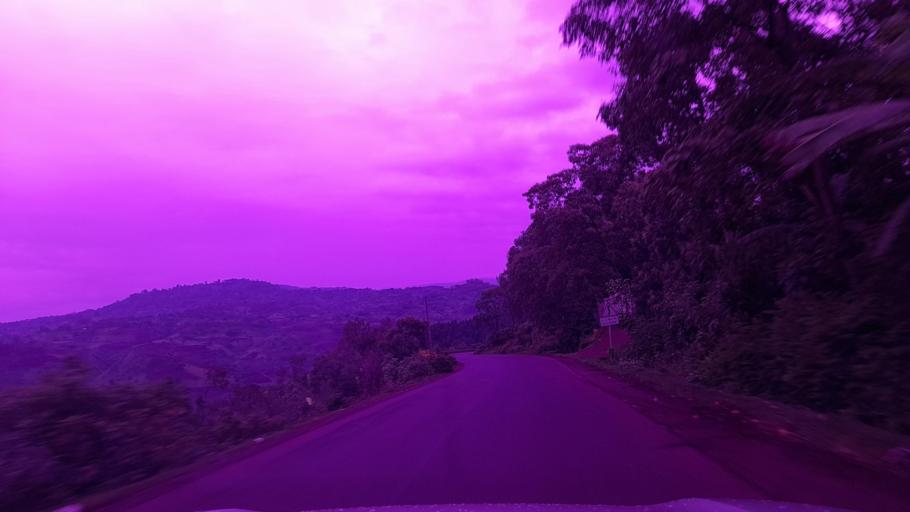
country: ET
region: Oromiya
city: Jima
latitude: 7.9292
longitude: 37.4295
